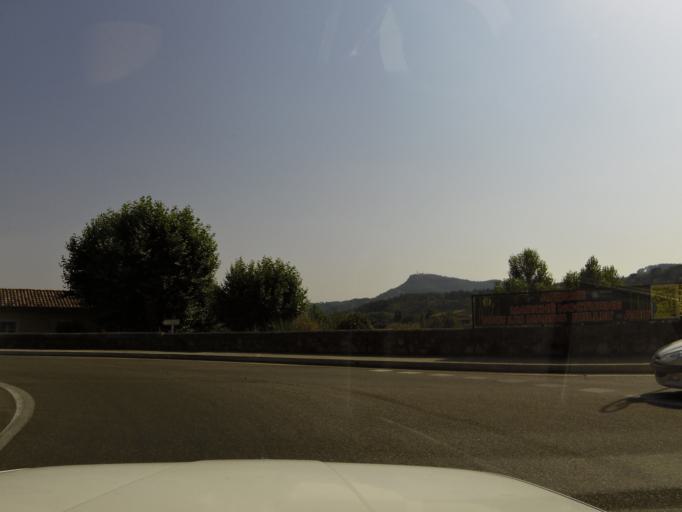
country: FR
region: Languedoc-Roussillon
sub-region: Departement du Gard
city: Anduze
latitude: 44.0555
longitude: 3.9893
